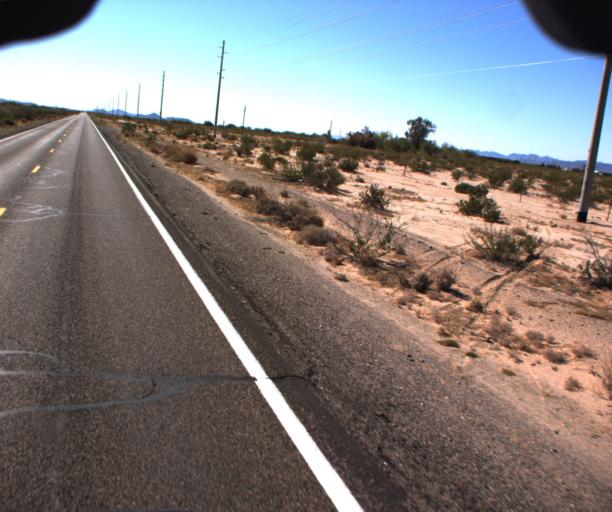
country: US
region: Arizona
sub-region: La Paz County
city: Salome
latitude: 33.8603
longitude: -113.9173
